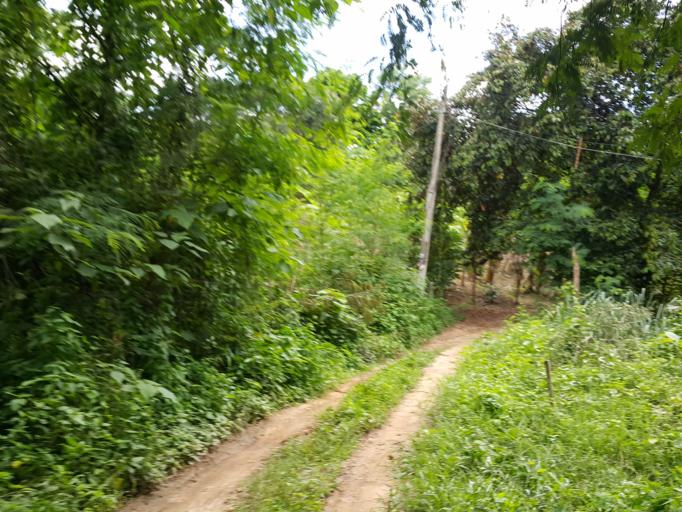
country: TH
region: Chiang Mai
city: San Sai
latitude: 18.9360
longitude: 98.9155
